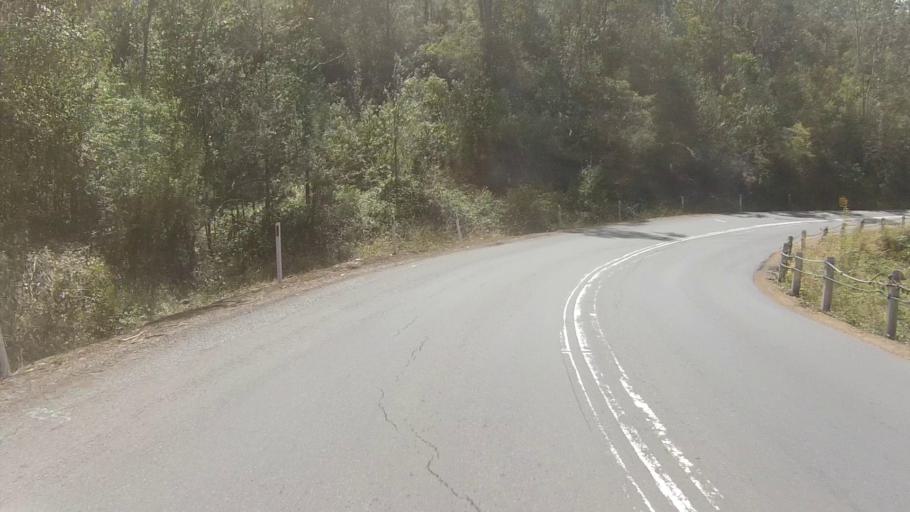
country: AU
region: Tasmania
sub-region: Kingborough
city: Taroona
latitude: -42.9597
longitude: 147.3314
